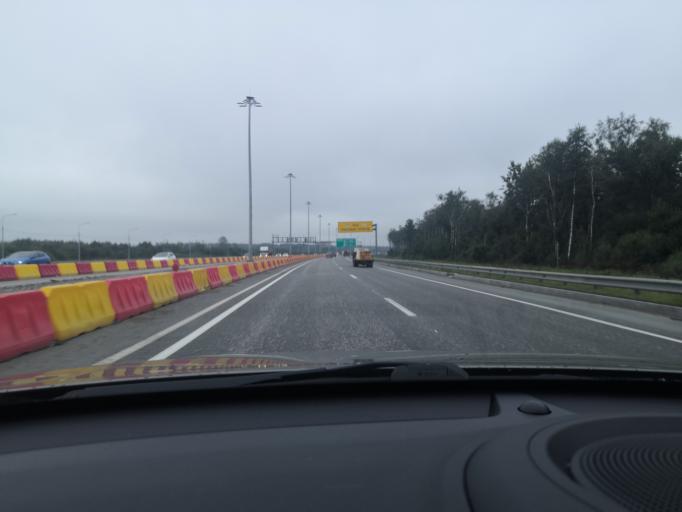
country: RU
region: St.-Petersburg
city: Levashovo
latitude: 60.0685
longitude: 30.1717
